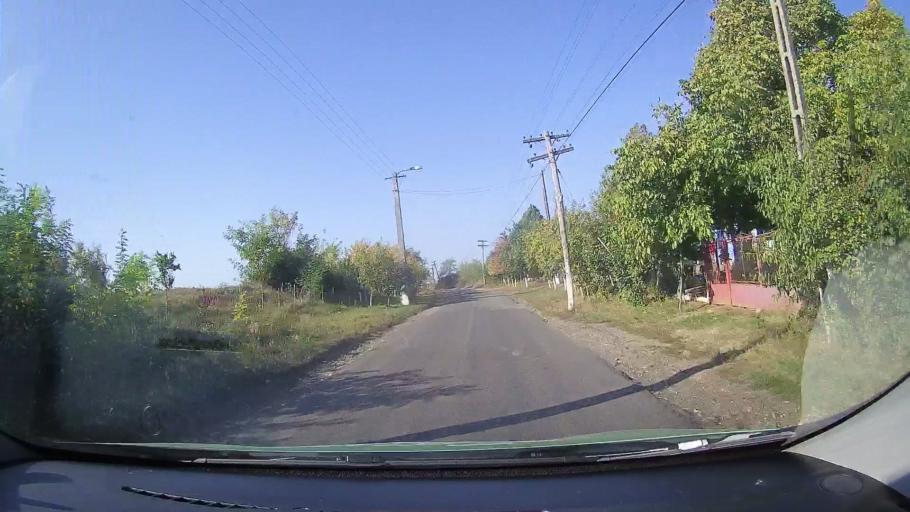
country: RO
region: Satu Mare
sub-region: Comuna Sauca
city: Sauca
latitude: 47.4709
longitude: 22.5170
